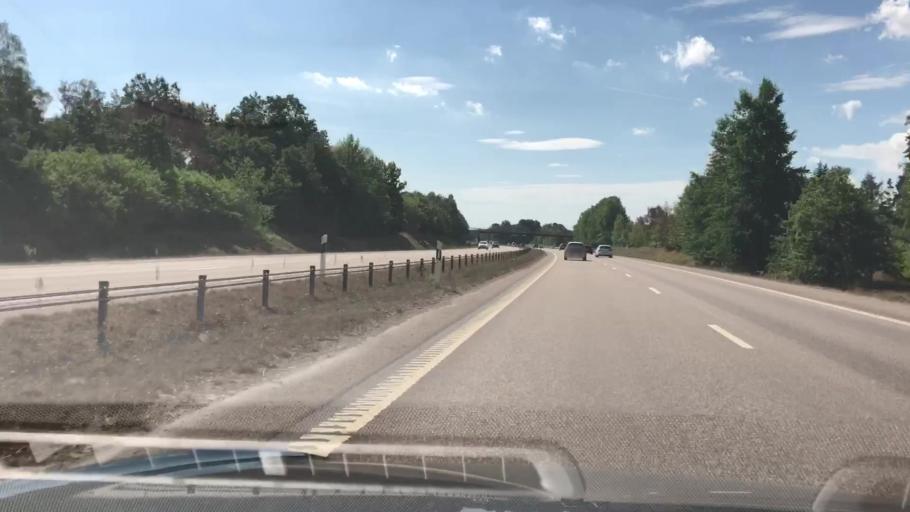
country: SE
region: Kalmar
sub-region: Kalmar Kommun
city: Lindsdal
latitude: 56.7054
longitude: 16.3123
